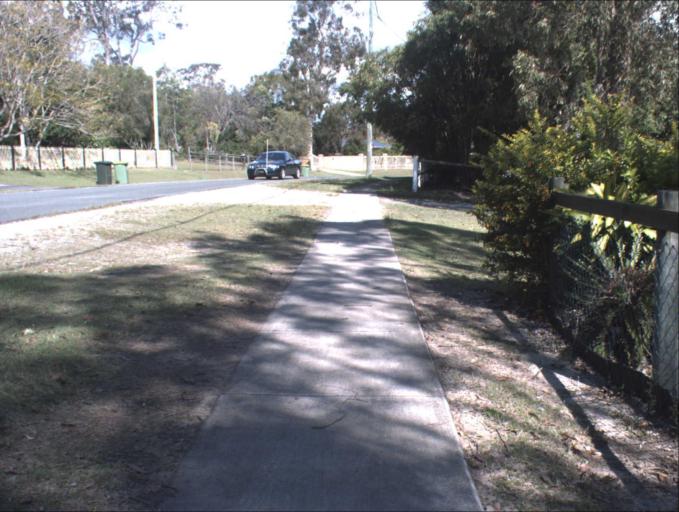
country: AU
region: Queensland
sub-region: Logan
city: Park Ridge South
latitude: -27.7408
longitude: 153.0320
